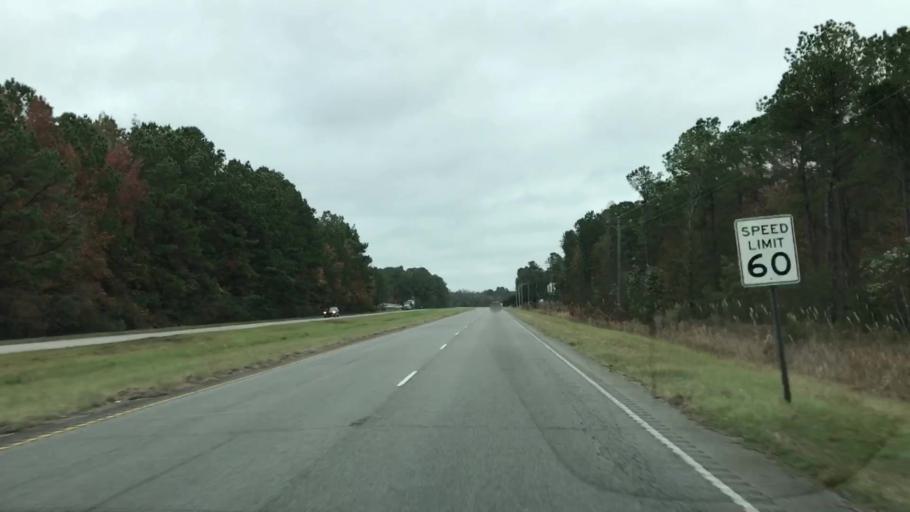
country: US
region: South Carolina
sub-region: Charleston County
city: Awendaw
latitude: 33.0216
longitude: -79.6315
